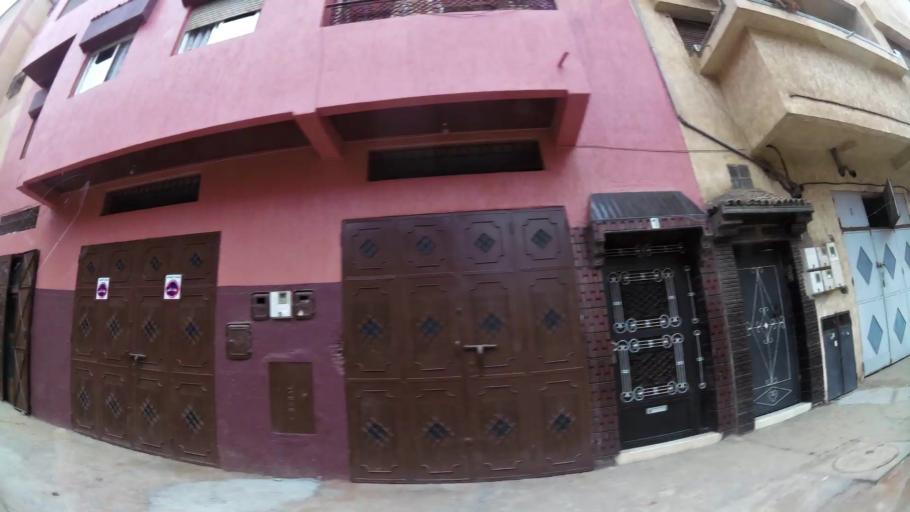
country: MA
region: Rabat-Sale-Zemmour-Zaer
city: Sale
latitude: 34.0379
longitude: -6.8056
